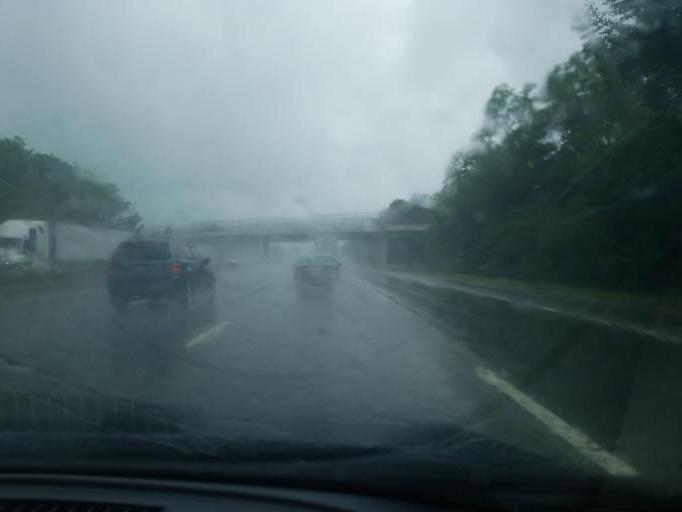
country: US
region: Ohio
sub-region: Hamilton County
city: Sixteen Mile Stand
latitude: 39.2809
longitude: -84.3342
